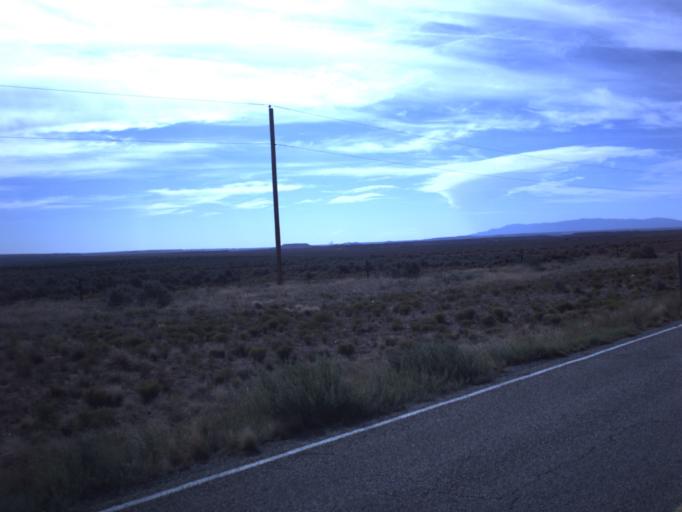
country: US
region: Utah
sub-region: San Juan County
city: Blanding
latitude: 37.4127
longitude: -109.3351
